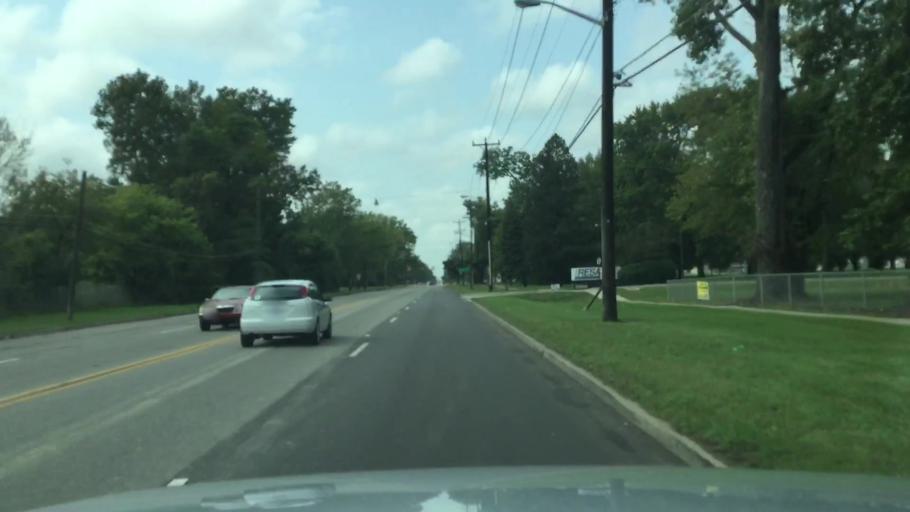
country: US
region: Michigan
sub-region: Wayne County
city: Wayne
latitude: 42.2671
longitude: -83.3687
